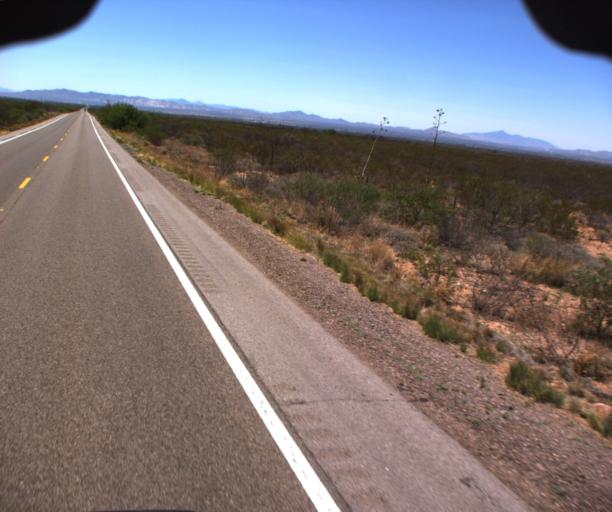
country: US
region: Arizona
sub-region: Cochise County
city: Douglas
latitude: 31.4343
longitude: -109.4811
